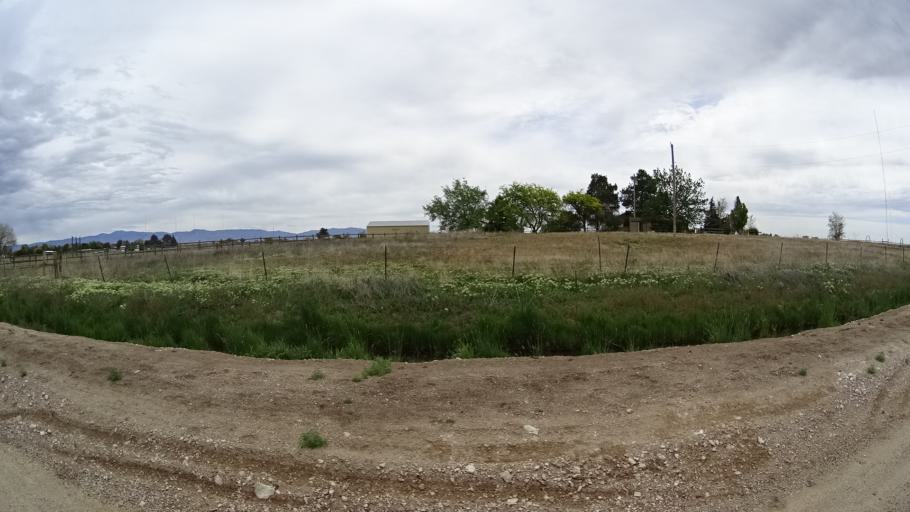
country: US
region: Idaho
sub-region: Ada County
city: Kuna
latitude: 43.5520
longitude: -116.4138
